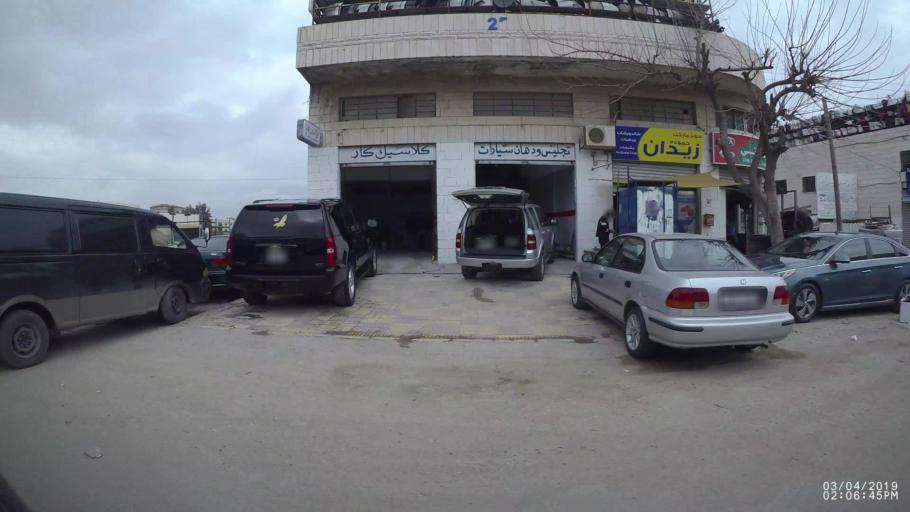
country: JO
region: Amman
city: Wadi as Sir
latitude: 31.9427
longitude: 35.8425
